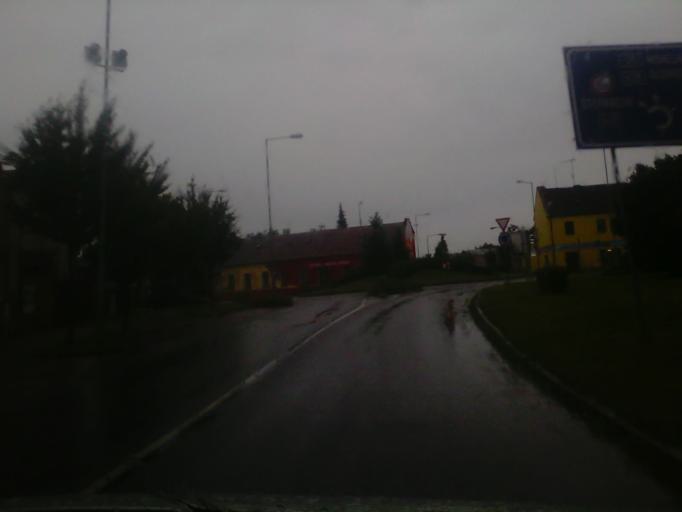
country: CZ
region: Olomoucky
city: Litovel
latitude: 49.7072
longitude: 17.0738
